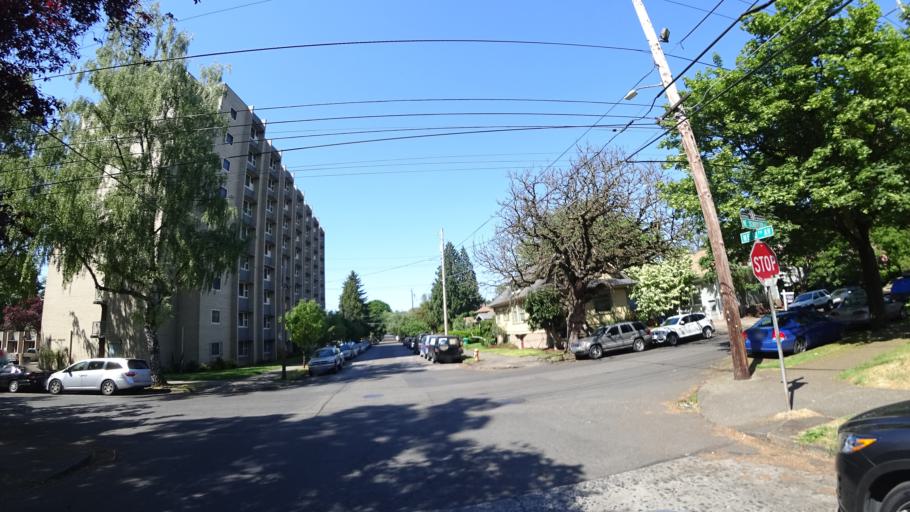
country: US
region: Oregon
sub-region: Multnomah County
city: Portland
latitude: 45.5356
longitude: -122.6556
